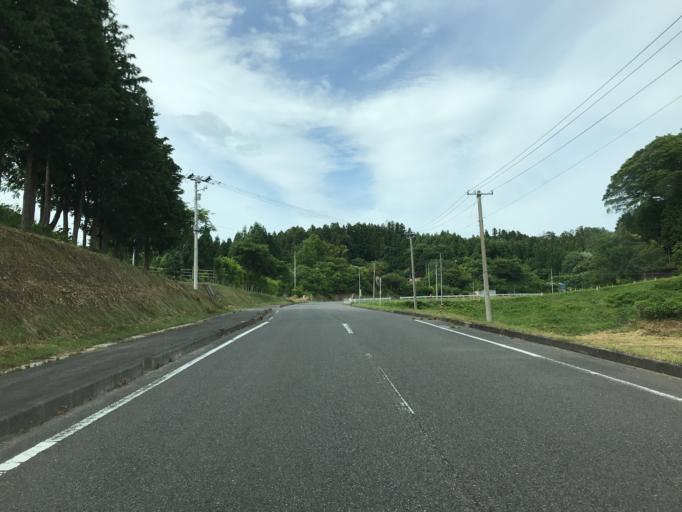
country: JP
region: Fukushima
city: Funehikimachi-funehiki
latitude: 37.5082
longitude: 140.5600
